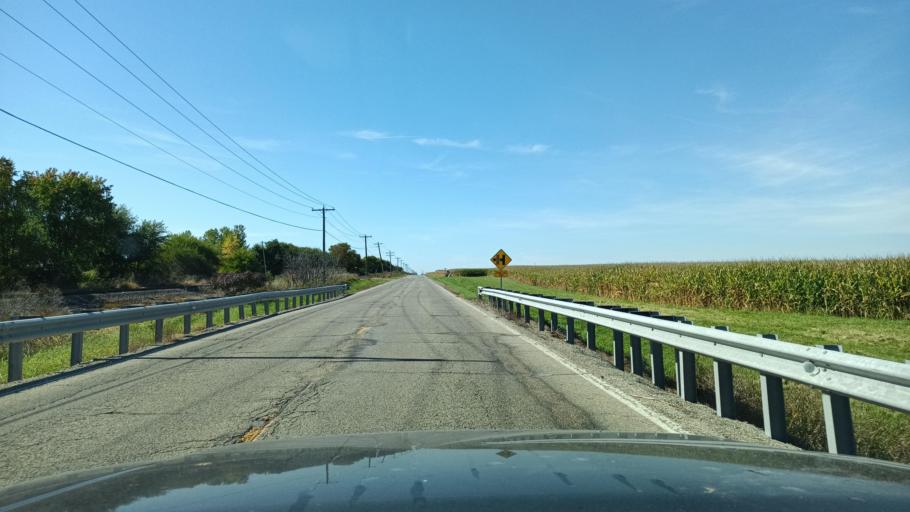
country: US
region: Illinois
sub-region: Champaign County
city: Mahomet
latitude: 40.1983
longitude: -88.4388
